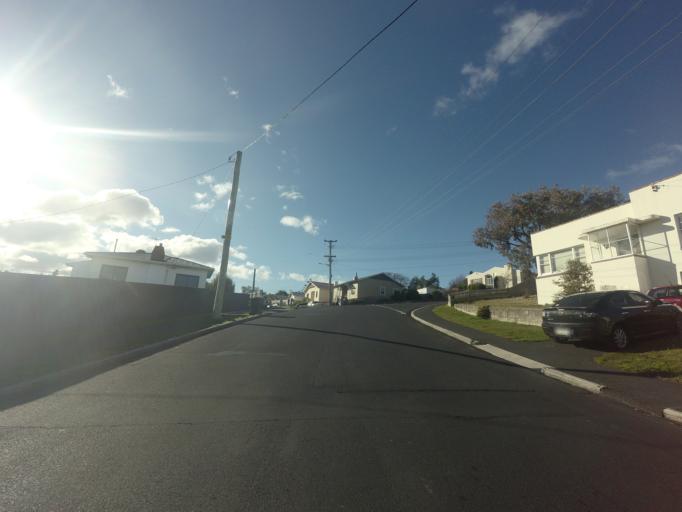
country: AU
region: Tasmania
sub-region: Glenorchy
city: Lutana
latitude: -42.8373
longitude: 147.3050
